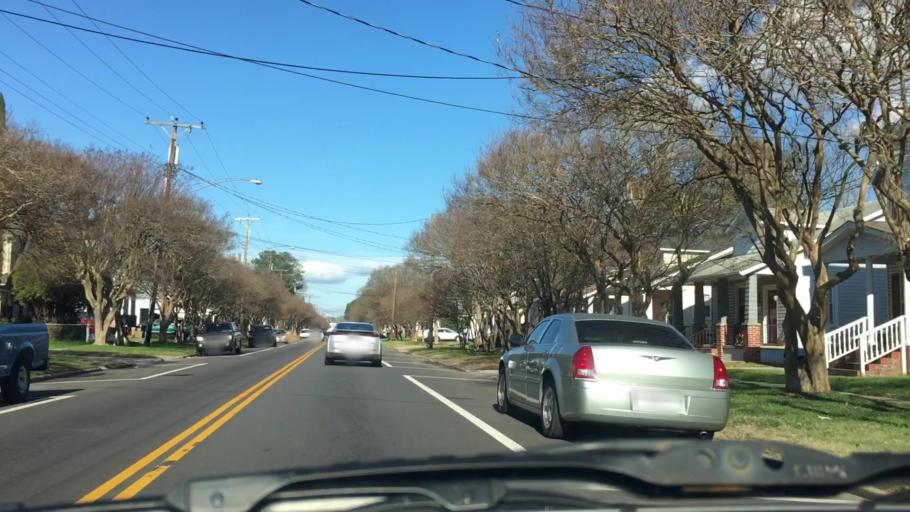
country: US
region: Virginia
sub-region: City of Norfolk
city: Norfolk
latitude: 36.8684
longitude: -76.2517
